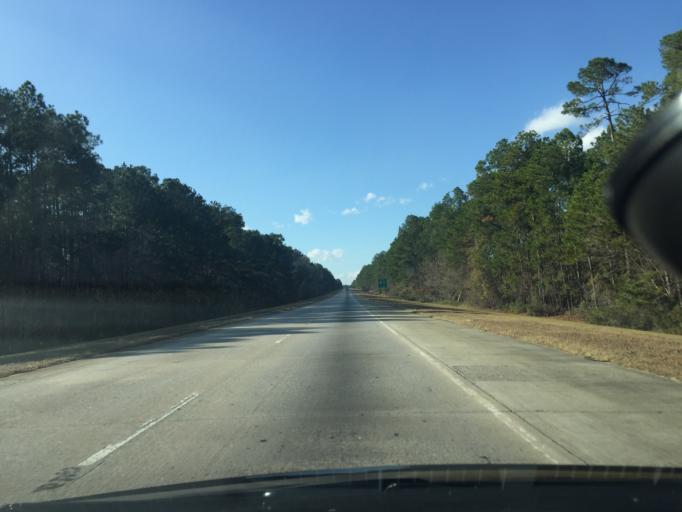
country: US
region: Georgia
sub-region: Treutlen County
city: Soperton
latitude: 32.4289
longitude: -82.4787
